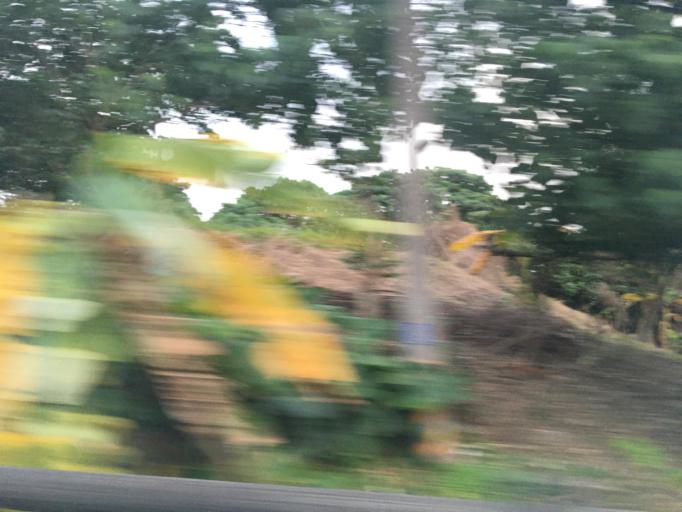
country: TW
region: Taiwan
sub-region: Yilan
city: Yilan
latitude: 24.7575
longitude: 121.7327
